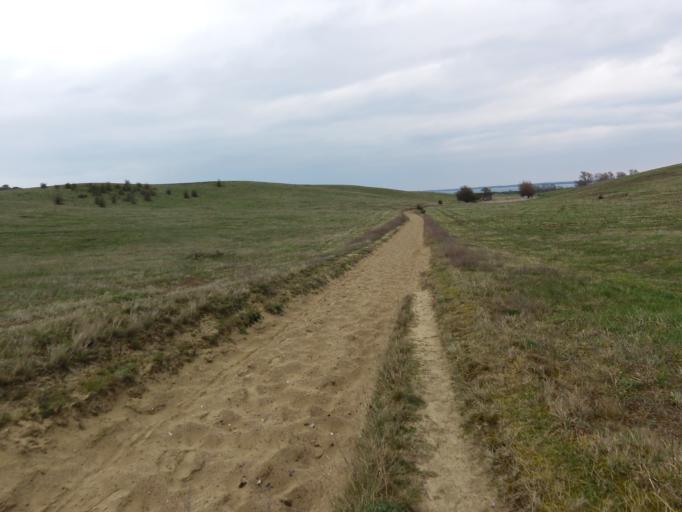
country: DE
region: Mecklenburg-Vorpommern
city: Hiddensee
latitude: 54.5978
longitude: 13.1240
